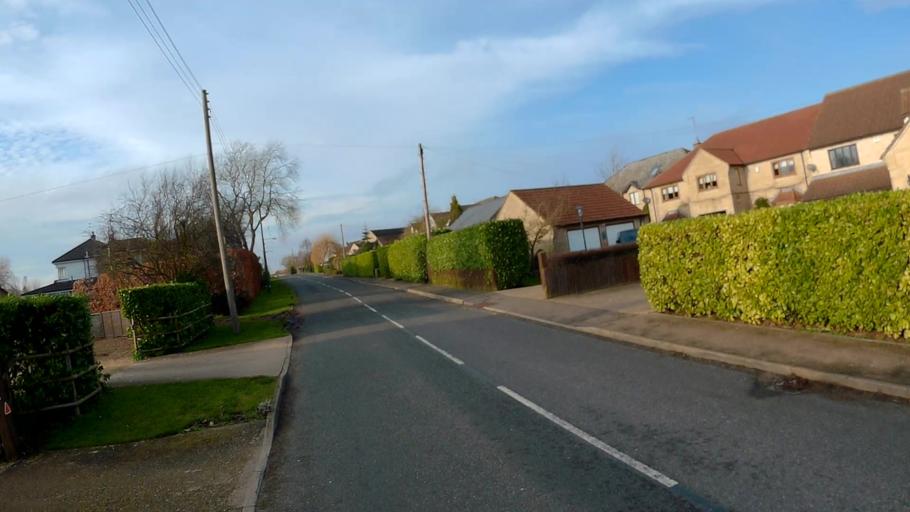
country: GB
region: England
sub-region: Lincolnshire
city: Bourne
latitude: 52.7368
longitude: -0.3906
